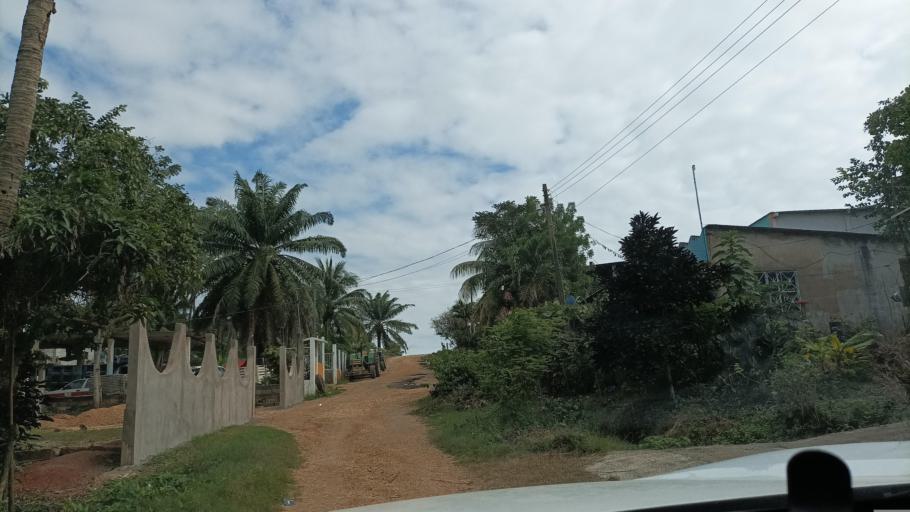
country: MX
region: Veracruz
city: Soconusco
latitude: 17.9615
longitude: -94.8150
